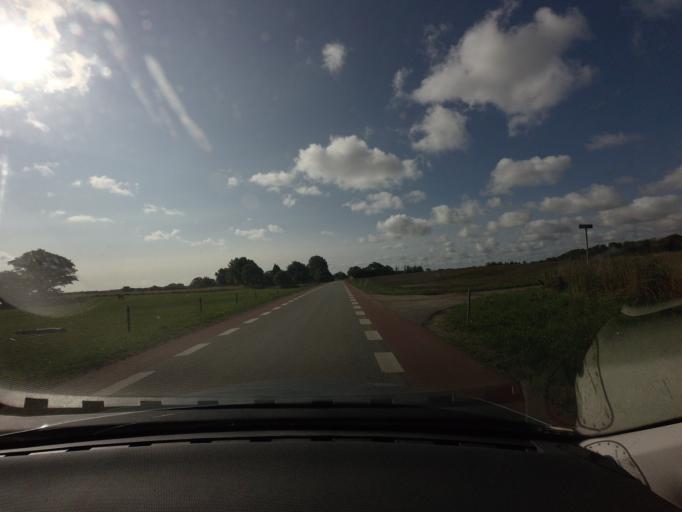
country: DK
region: Zealand
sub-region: Vordingborg Kommune
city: Praesto
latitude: 55.1353
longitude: 12.0185
